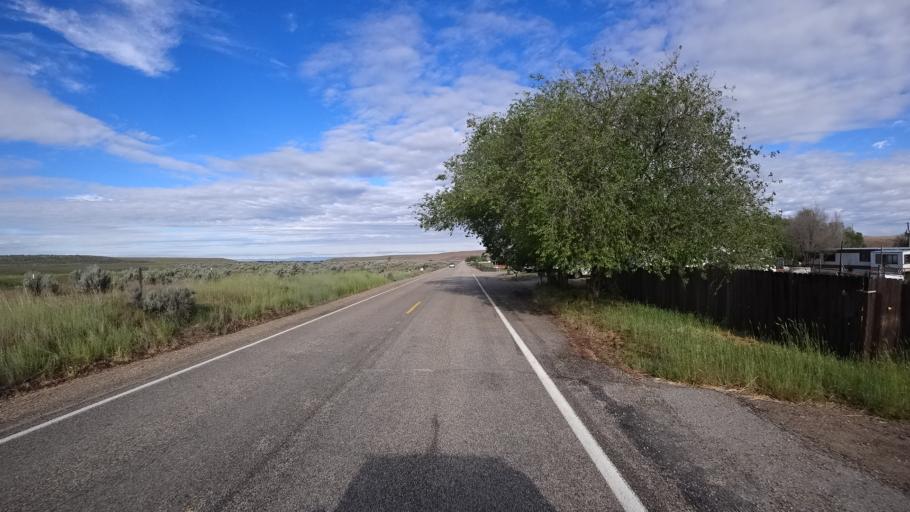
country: US
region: Idaho
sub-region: Ada County
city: Star
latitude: 43.7718
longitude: -116.4797
